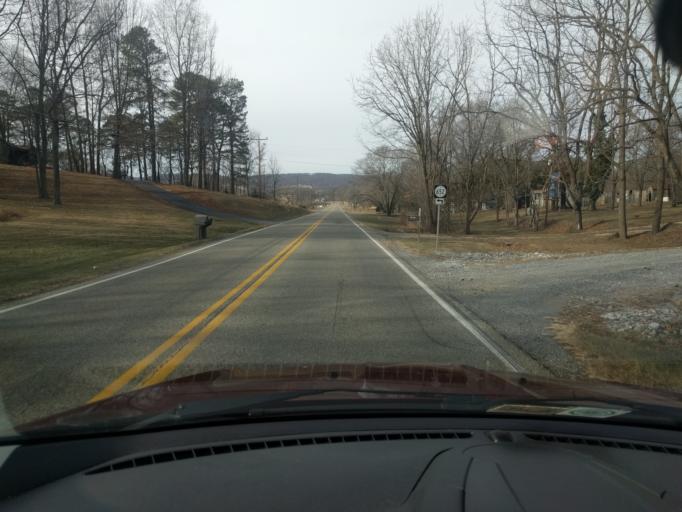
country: US
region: Virginia
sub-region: Augusta County
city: Stuarts Draft
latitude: 38.0383
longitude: -79.0767
